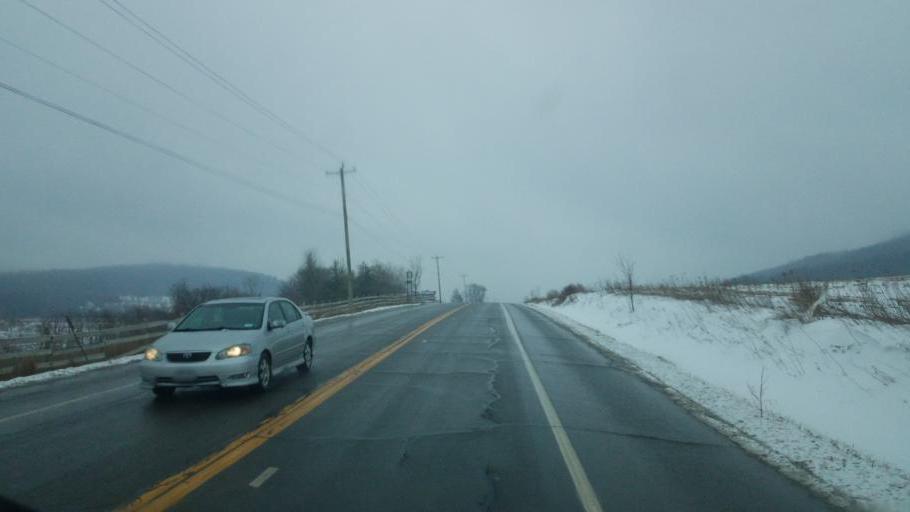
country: US
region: New York
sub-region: Steuben County
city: Canisteo
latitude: 42.1126
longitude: -77.4892
